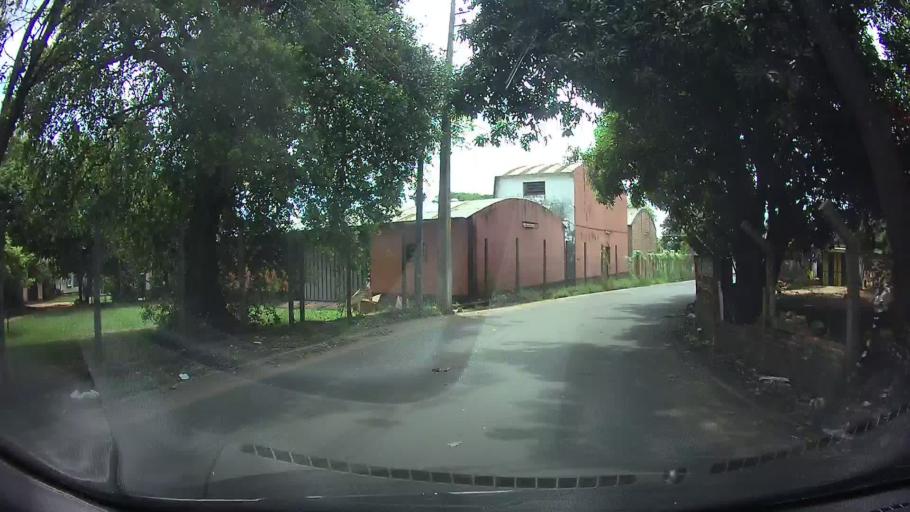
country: PY
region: Central
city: Fernando de la Mora
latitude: -25.3233
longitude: -57.5478
